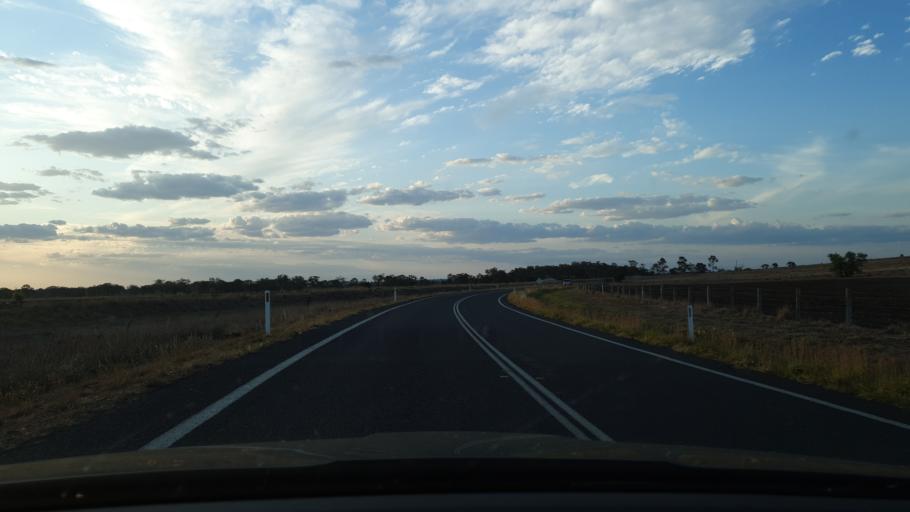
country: AU
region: Queensland
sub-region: Southern Downs
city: Warwick
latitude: -28.1817
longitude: 151.9787
